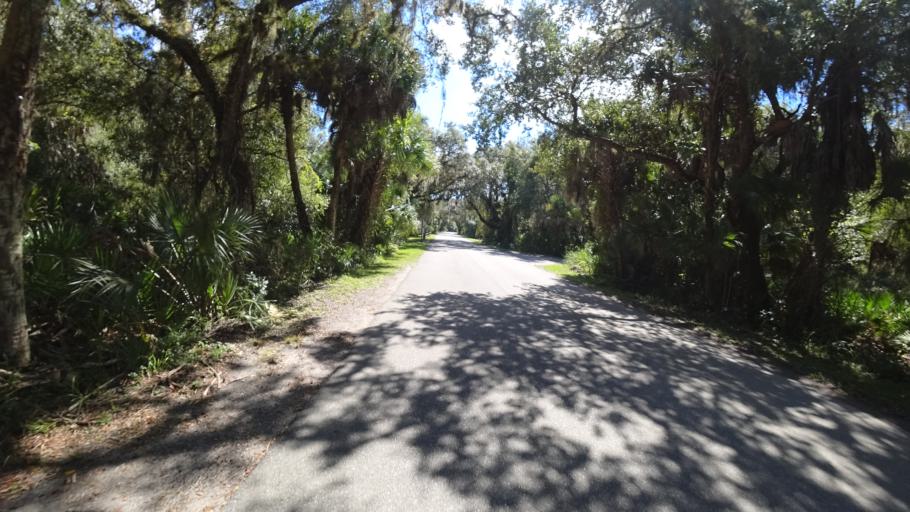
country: US
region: Florida
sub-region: Sarasota County
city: Lake Sarasota
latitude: 27.2426
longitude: -82.3142
